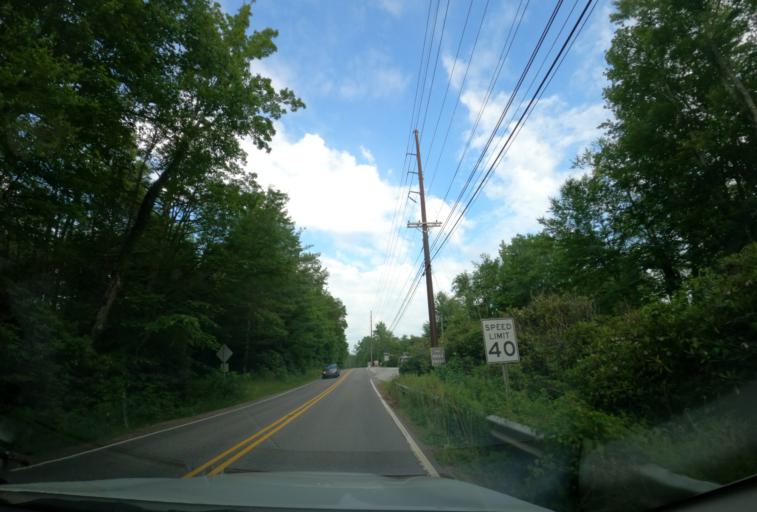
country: US
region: North Carolina
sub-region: Jackson County
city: Cullowhee
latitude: 35.0886
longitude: -83.1706
